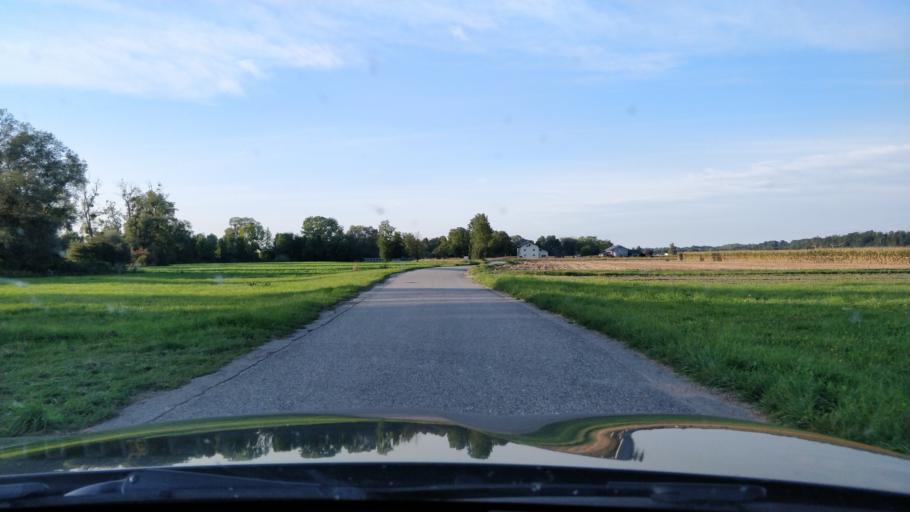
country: AT
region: Upper Austria
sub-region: Politischer Bezirk Braunau am Inn
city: Braunau am Inn
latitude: 48.1673
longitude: 13.1276
